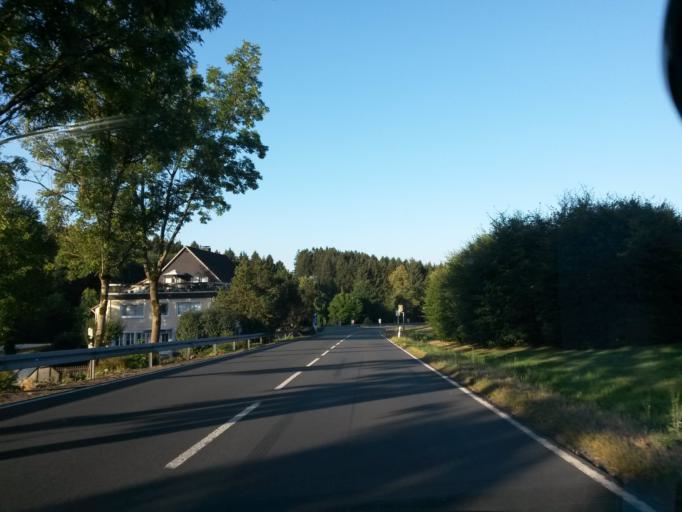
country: DE
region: North Rhine-Westphalia
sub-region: Regierungsbezirk Koln
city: Marienheide
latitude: 51.1159
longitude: 7.5489
